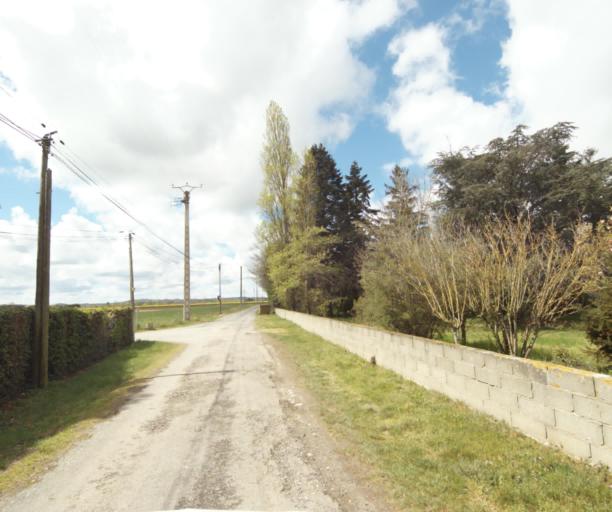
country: FR
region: Midi-Pyrenees
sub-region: Departement de l'Ariege
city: Saverdun
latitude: 43.2450
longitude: 1.6096
